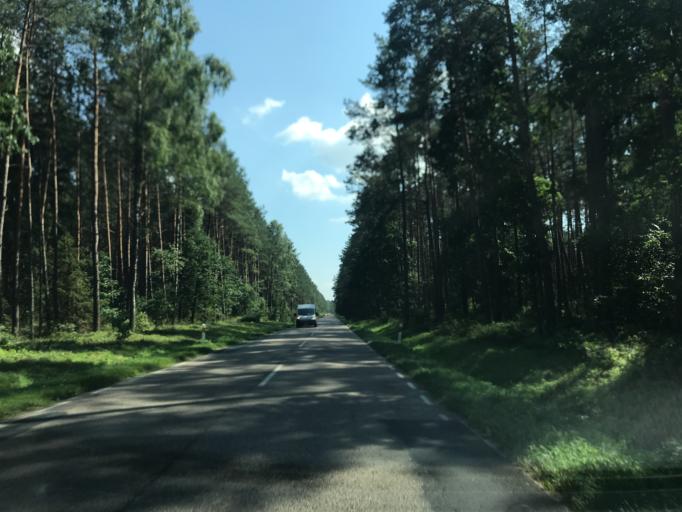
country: PL
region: Warmian-Masurian Voivodeship
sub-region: Powiat dzialdowski
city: Lidzbark
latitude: 53.2166
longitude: 19.8393
